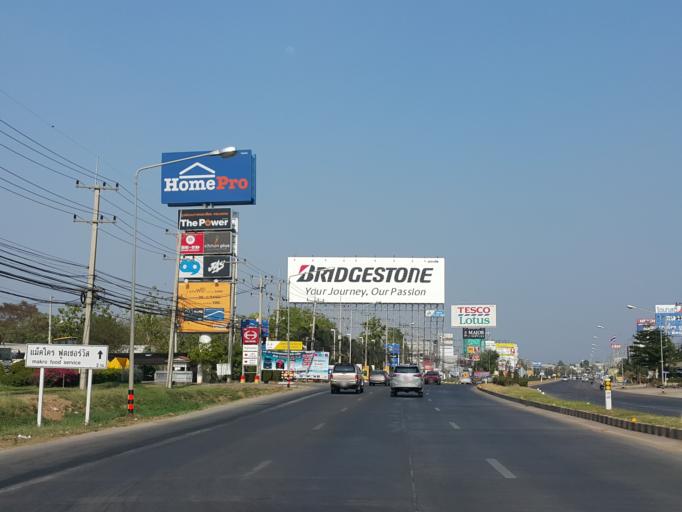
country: TH
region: Phitsanulok
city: Phitsanulok
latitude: 16.8179
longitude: 100.2965
